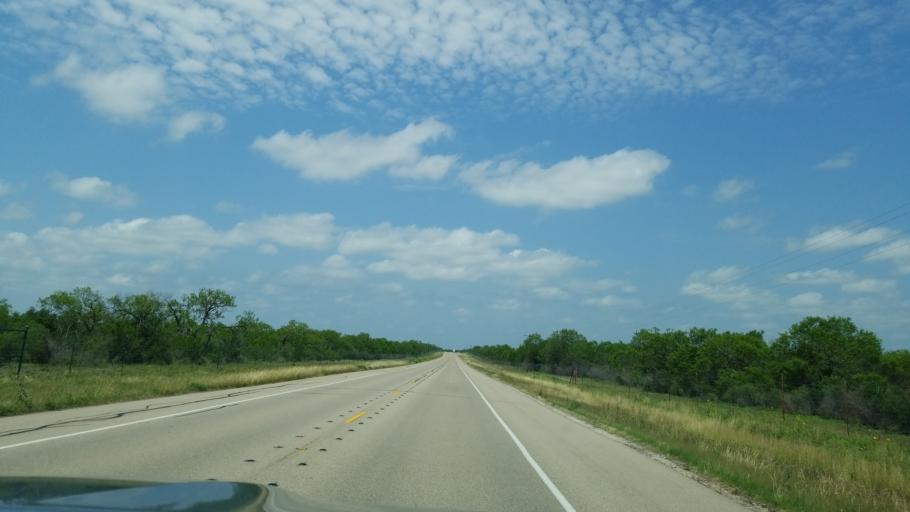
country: US
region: Texas
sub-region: Frio County
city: Pearsall
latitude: 29.0077
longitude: -99.1887
